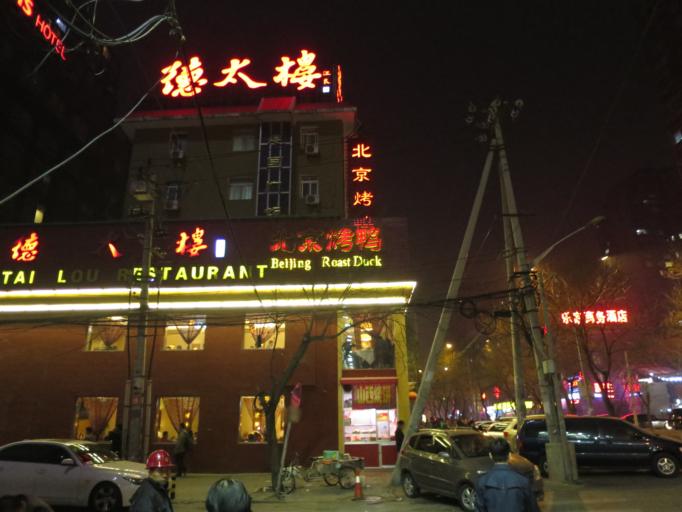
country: CN
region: Beijing
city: Chaowai
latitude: 39.9060
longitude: 116.4378
